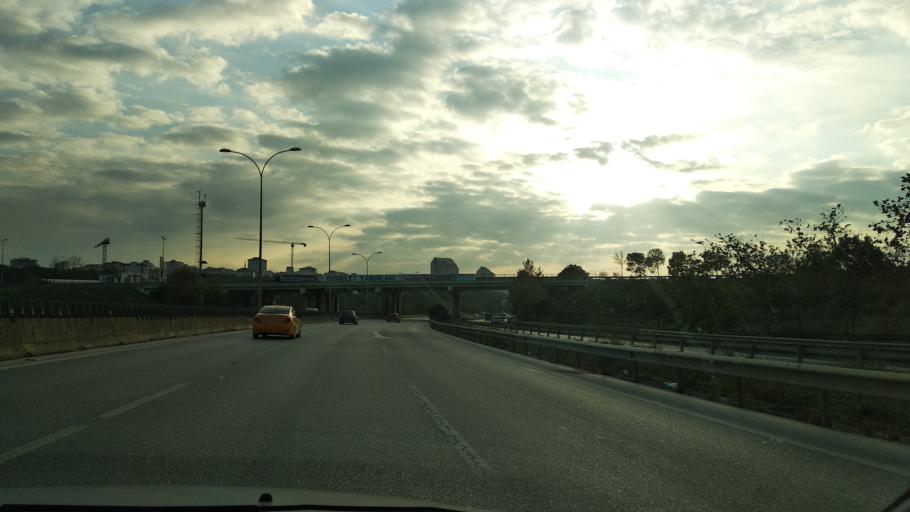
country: TR
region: Istanbul
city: Icmeler
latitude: 40.8798
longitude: 29.3153
